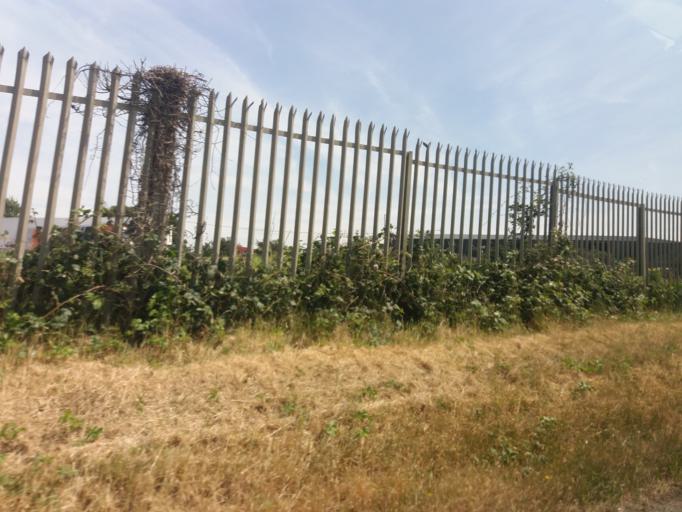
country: IE
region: Leinster
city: Lusk
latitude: 53.5344
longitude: -6.1962
